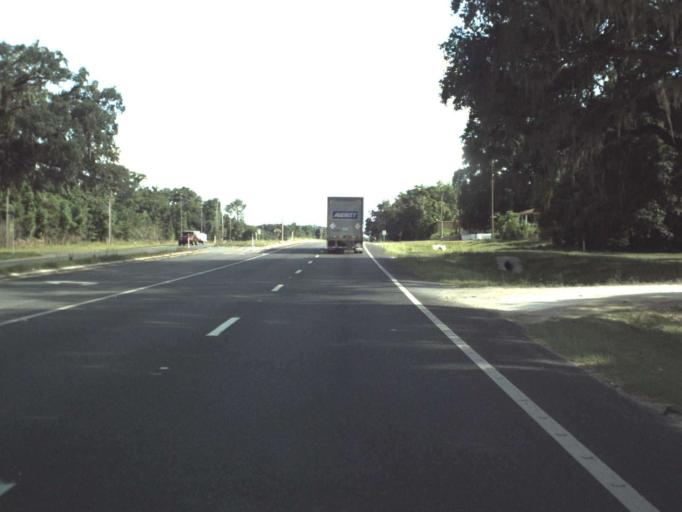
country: US
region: Florida
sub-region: Sumter County
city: Wildwood
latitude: 28.8916
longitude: -82.0371
